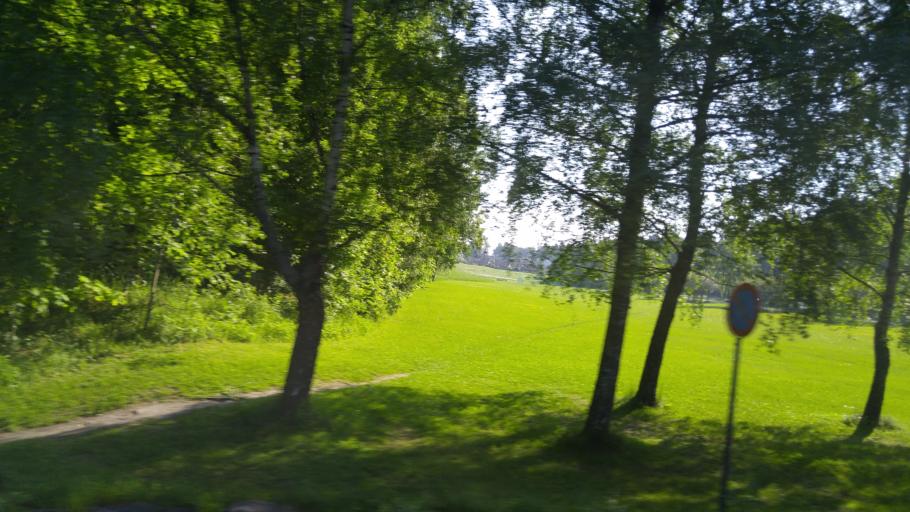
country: NO
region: Akershus
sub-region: Baerum
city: Sandvika
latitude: 59.8905
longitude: 10.5582
